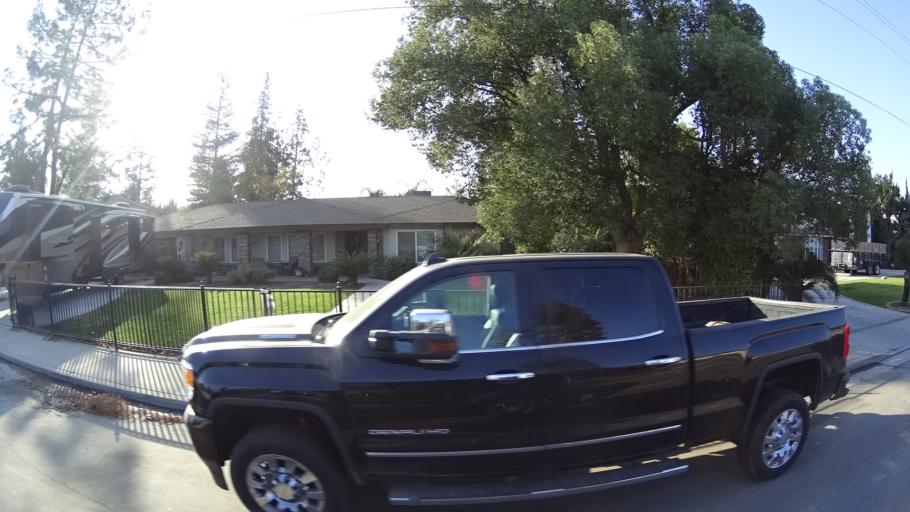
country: US
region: California
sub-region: Kern County
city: Rosedale
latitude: 35.3762
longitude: -119.1350
